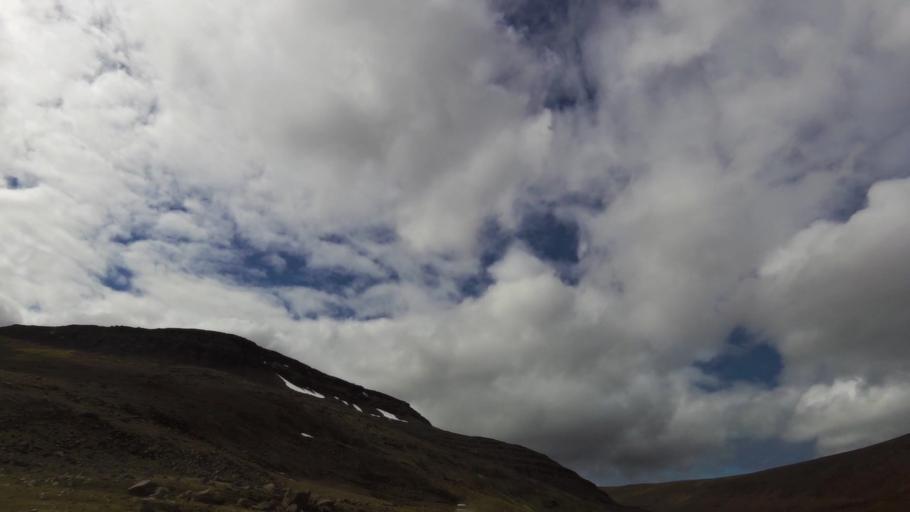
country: IS
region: Westfjords
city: Isafjoerdur
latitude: 66.1651
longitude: -23.3356
